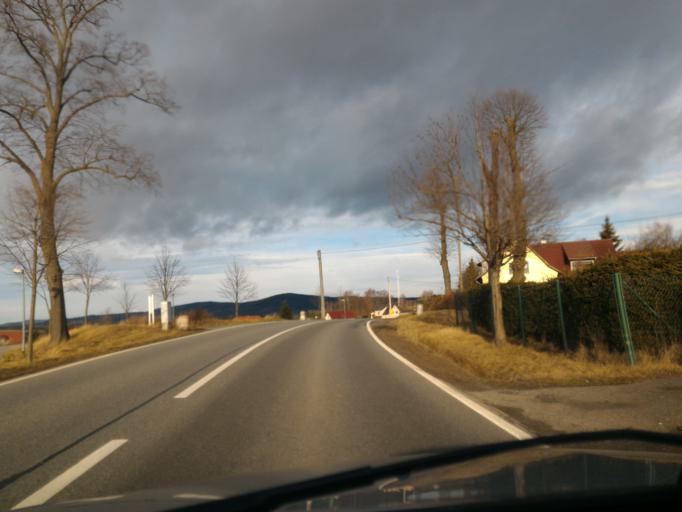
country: DE
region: Saxony
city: Oppach
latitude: 51.0469
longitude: 14.5121
